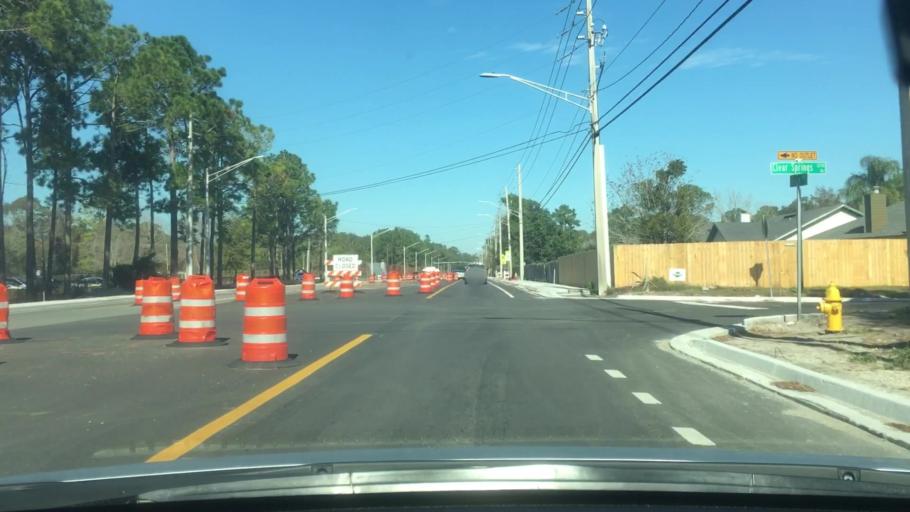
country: US
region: Florida
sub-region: Duval County
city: Atlantic Beach
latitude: 30.3209
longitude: -81.4726
